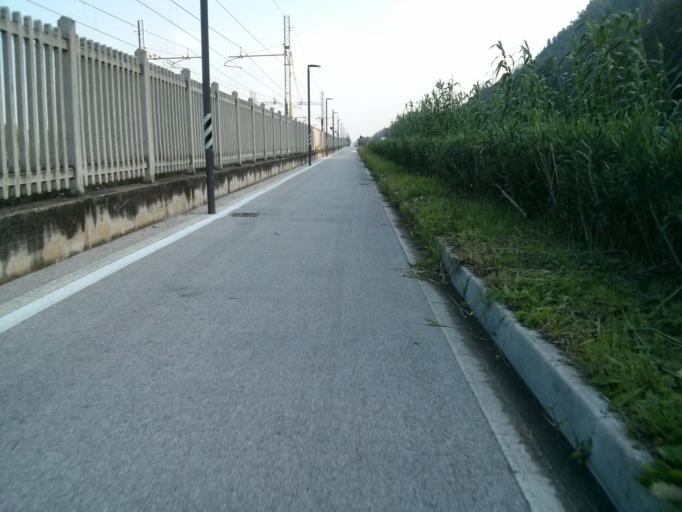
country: IT
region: The Marches
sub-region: Provincia di Pesaro e Urbino
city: Fenile
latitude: 43.8767
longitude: 12.9682
